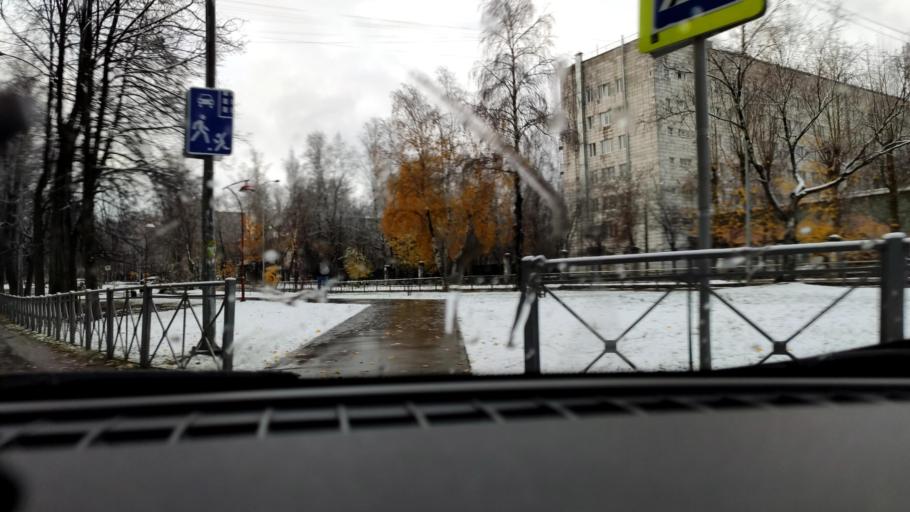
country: RU
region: Perm
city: Kondratovo
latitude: 57.9817
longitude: 56.1813
